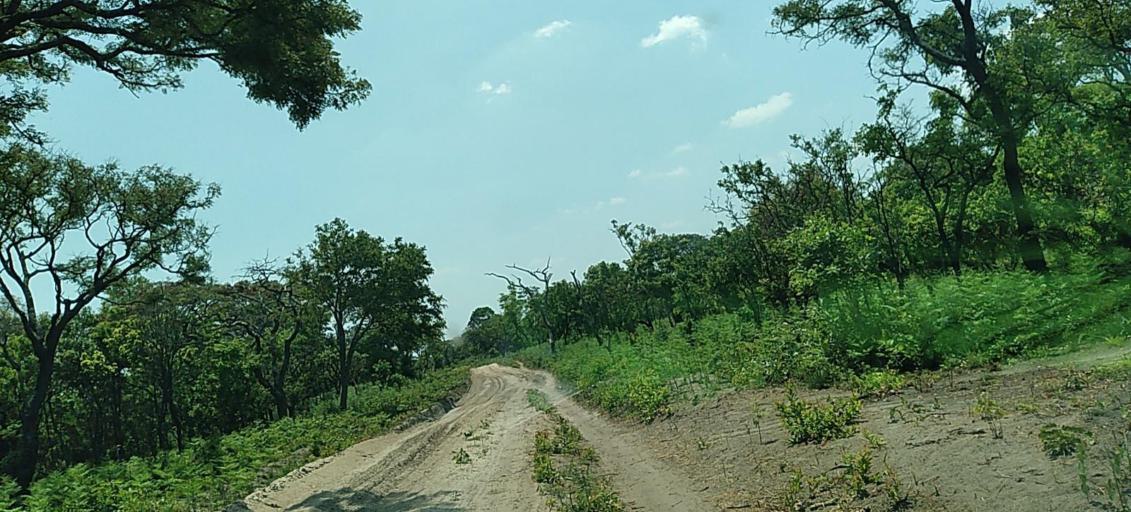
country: CD
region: Katanga
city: Kolwezi
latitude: -11.2985
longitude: 25.2265
